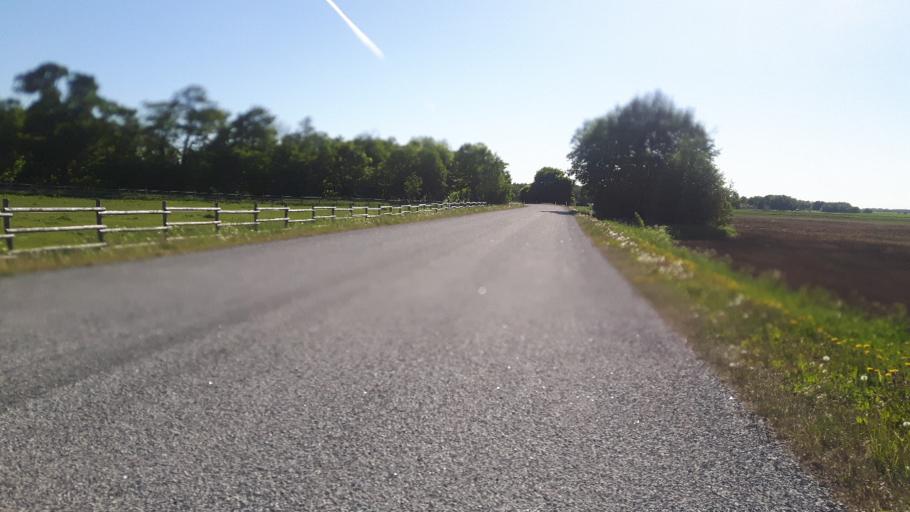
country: EE
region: Ida-Virumaa
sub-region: Kohtla-Jaerve linn
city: Kohtla-Jarve
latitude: 59.4392
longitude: 27.3008
